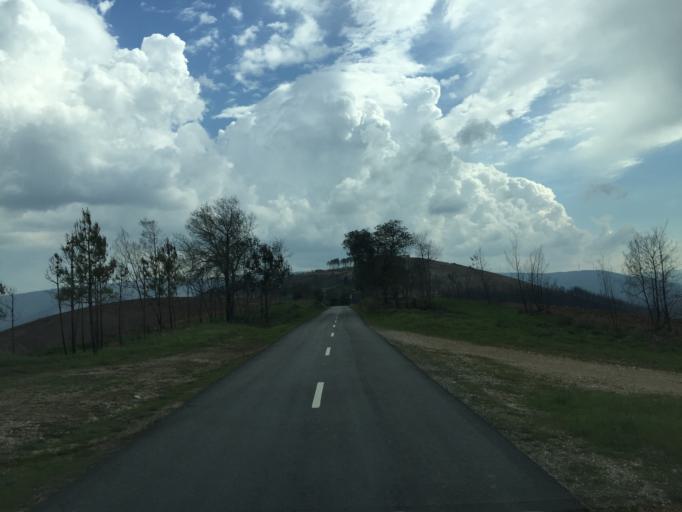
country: PT
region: Coimbra
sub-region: Arganil
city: Arganil
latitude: 40.1704
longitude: -7.9716
